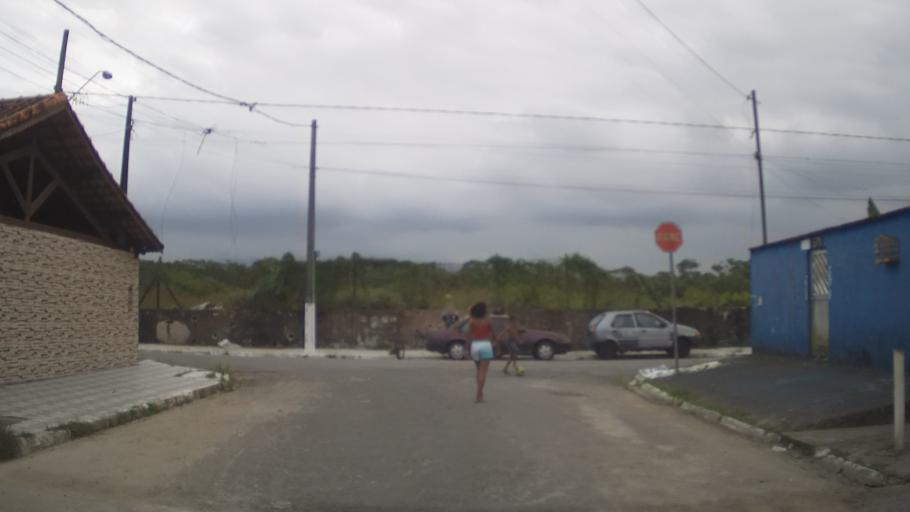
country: BR
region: Sao Paulo
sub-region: Praia Grande
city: Praia Grande
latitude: -24.0048
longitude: -46.4568
